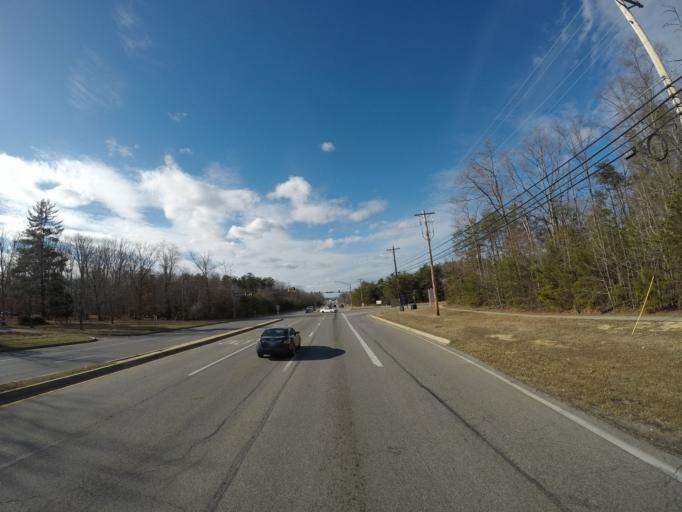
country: US
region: Maryland
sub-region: Charles County
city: Saint Charles
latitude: 38.6049
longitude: -76.9498
